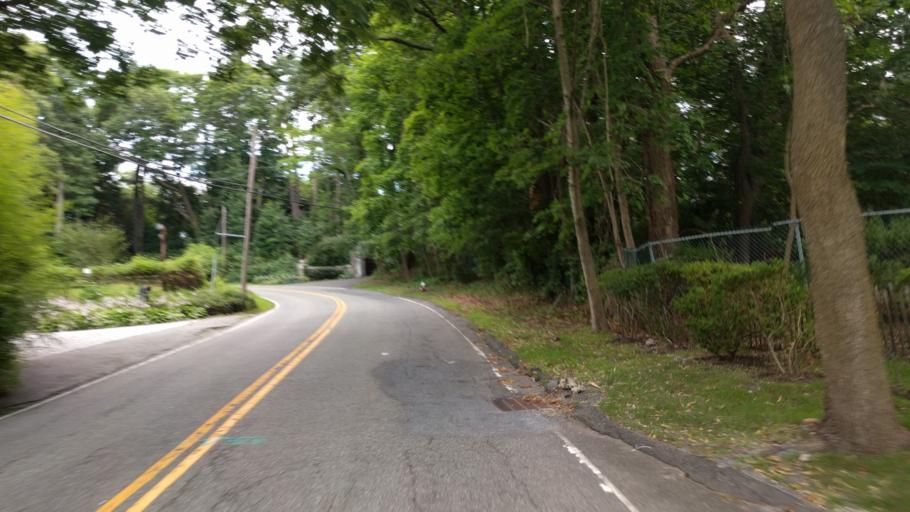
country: US
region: New York
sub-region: Nassau County
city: Oyster Bay Cove
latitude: 40.8675
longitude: -73.5206
